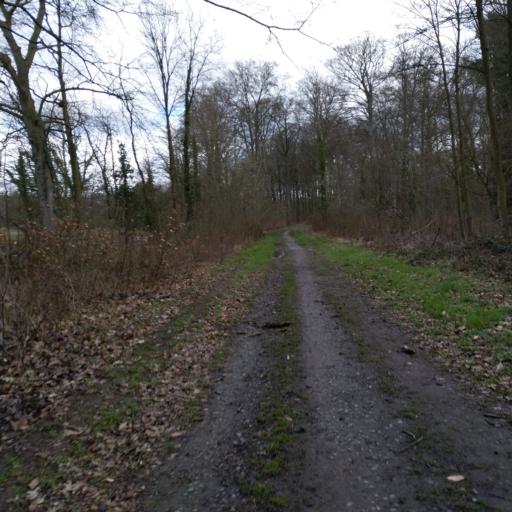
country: BE
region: Wallonia
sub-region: Province du Hainaut
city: Mons
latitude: 50.4864
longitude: 3.9233
